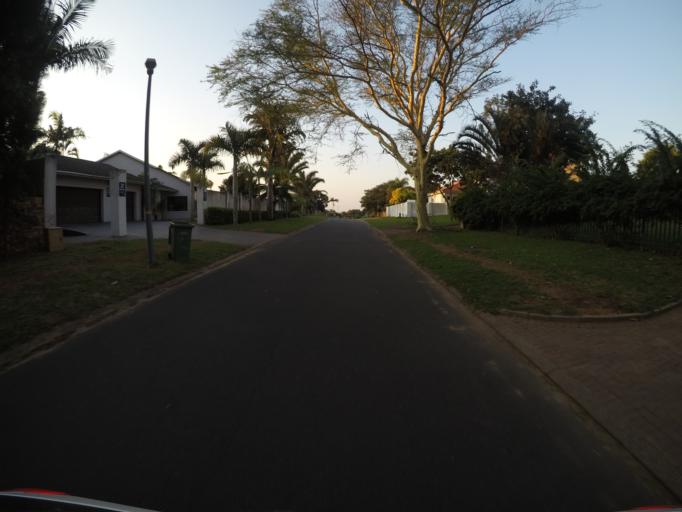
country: ZA
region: KwaZulu-Natal
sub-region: uThungulu District Municipality
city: Richards Bay
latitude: -28.7675
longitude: 32.1173
